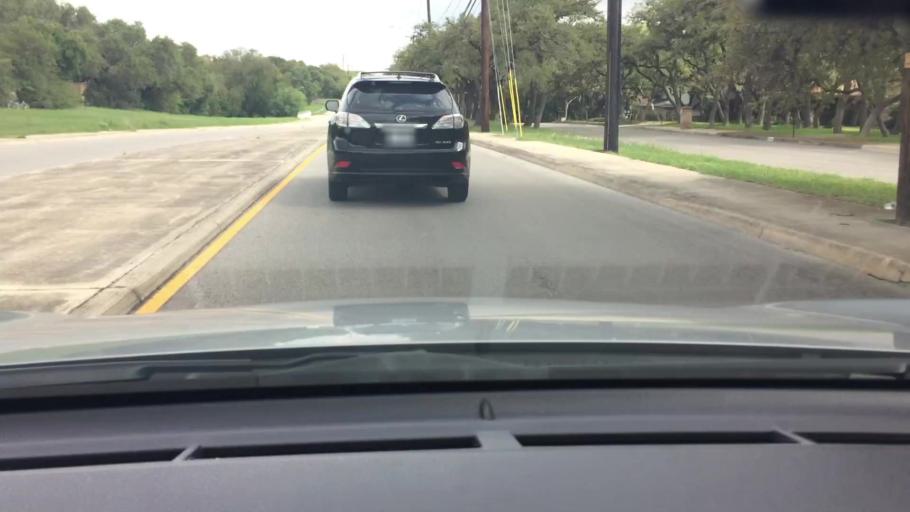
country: US
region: Texas
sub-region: Bexar County
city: Castle Hills
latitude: 29.5496
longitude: -98.5391
